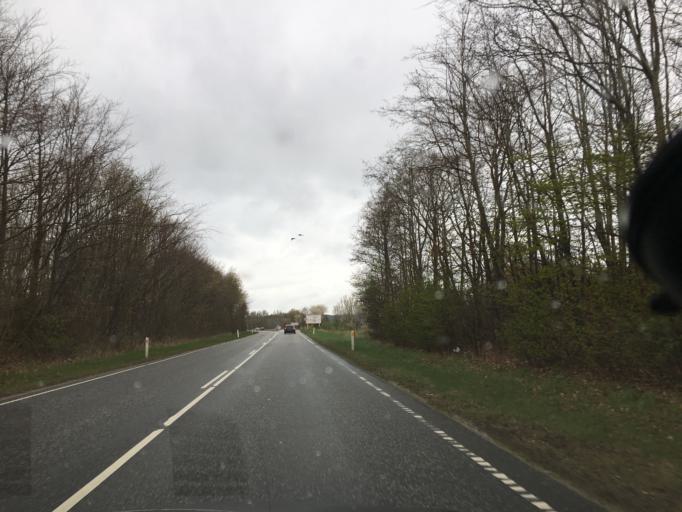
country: DK
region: Zealand
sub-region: Odsherred Kommune
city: Hojby
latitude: 55.9188
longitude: 11.5460
